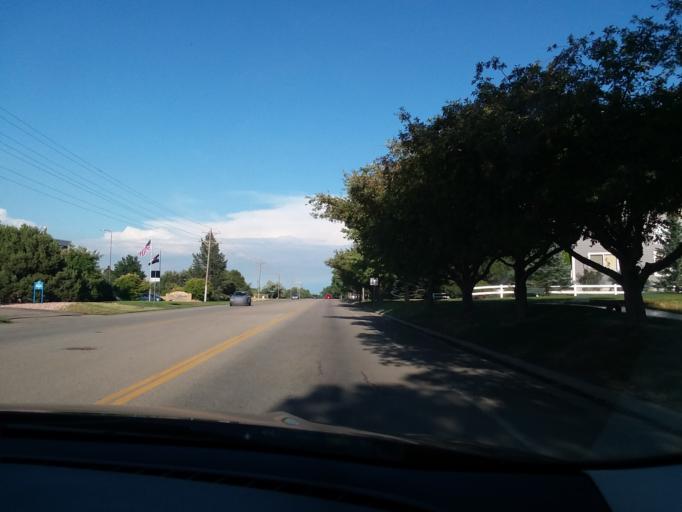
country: US
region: Colorado
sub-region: Larimer County
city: Fort Collins
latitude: 40.4946
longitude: -105.0868
